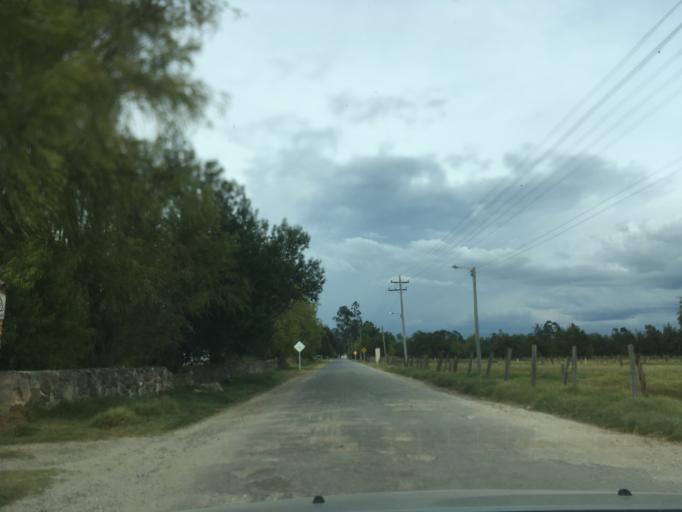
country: CO
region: Boyaca
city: Firavitoba
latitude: 5.6493
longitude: -72.9899
